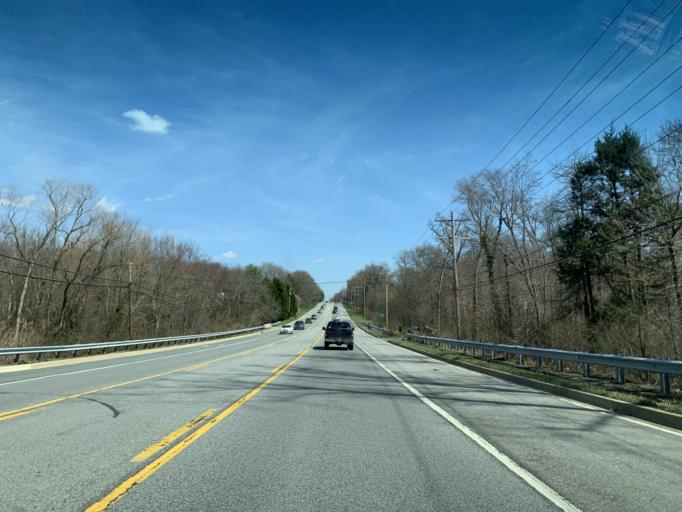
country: US
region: Delaware
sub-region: New Castle County
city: Bear
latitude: 39.6563
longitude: -75.6761
